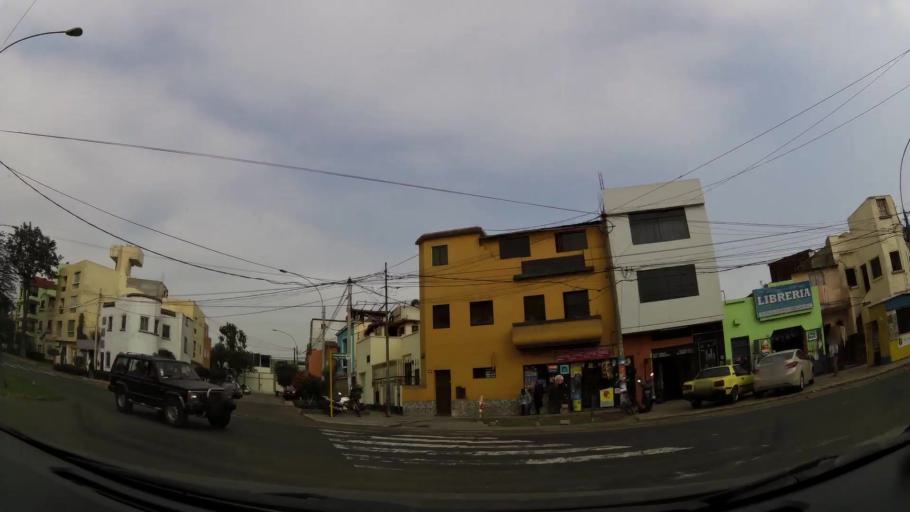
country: PE
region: Lima
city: Lima
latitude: -12.0772
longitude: -77.0471
